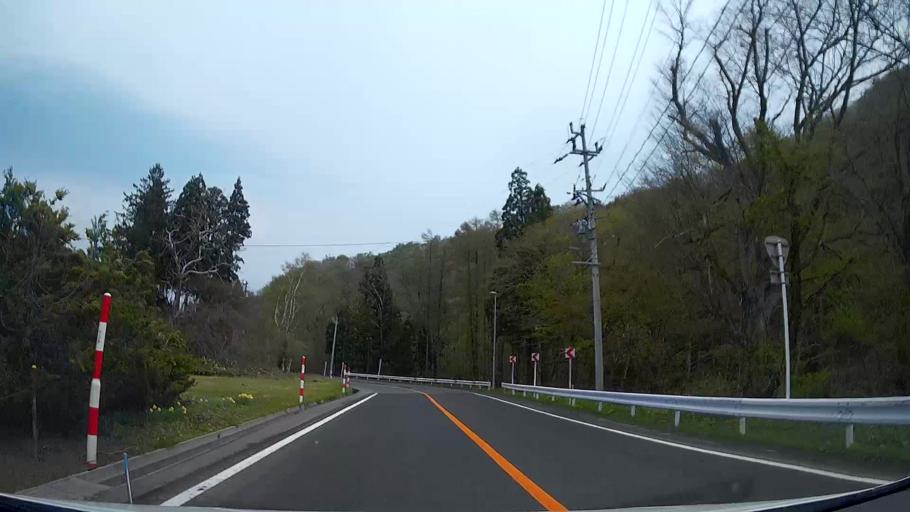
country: JP
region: Akita
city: Hanawa
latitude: 40.3705
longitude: 140.8732
